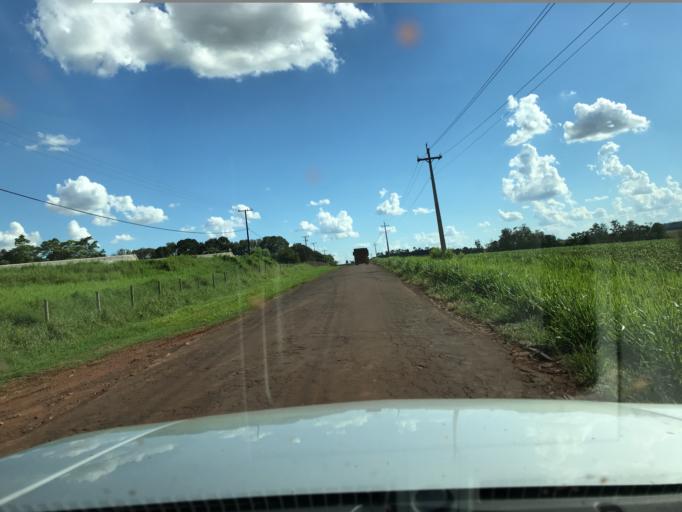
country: BR
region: Parana
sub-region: Palotina
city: Palotina
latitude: -24.2600
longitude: -53.7995
